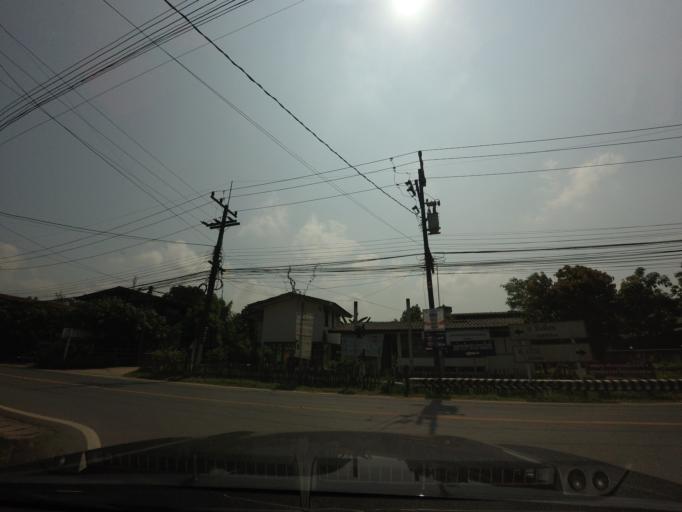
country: TH
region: Nan
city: Nan
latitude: 18.8588
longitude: 100.8179
